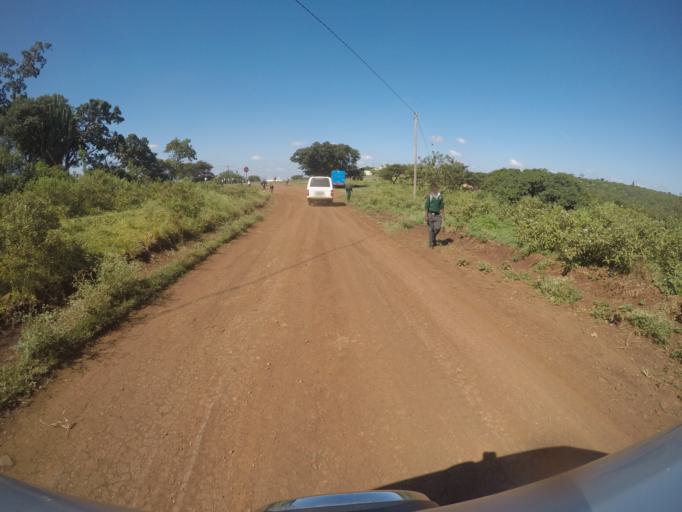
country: ZA
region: KwaZulu-Natal
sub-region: uThungulu District Municipality
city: Empangeni
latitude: -28.5626
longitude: 31.7030
